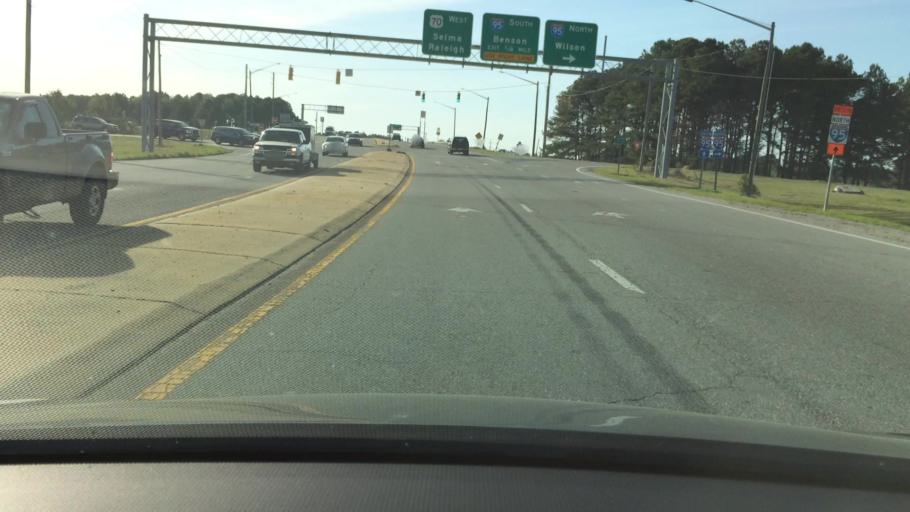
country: US
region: North Carolina
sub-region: Johnston County
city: Selma
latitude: 35.5185
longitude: -78.2868
